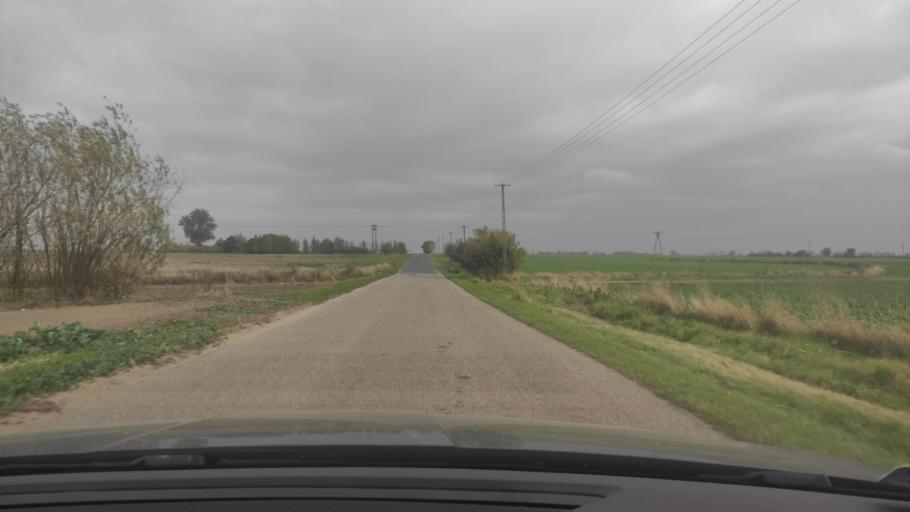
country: PL
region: Greater Poland Voivodeship
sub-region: Powiat poznanski
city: Kostrzyn
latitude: 52.4438
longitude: 17.1866
